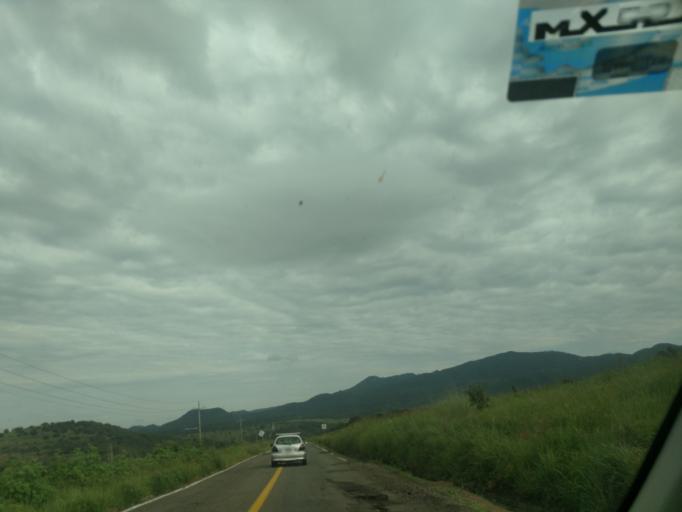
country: MX
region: Jalisco
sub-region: Atengo
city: Soyatlan del Oro
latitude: 20.5447
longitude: -104.2970
